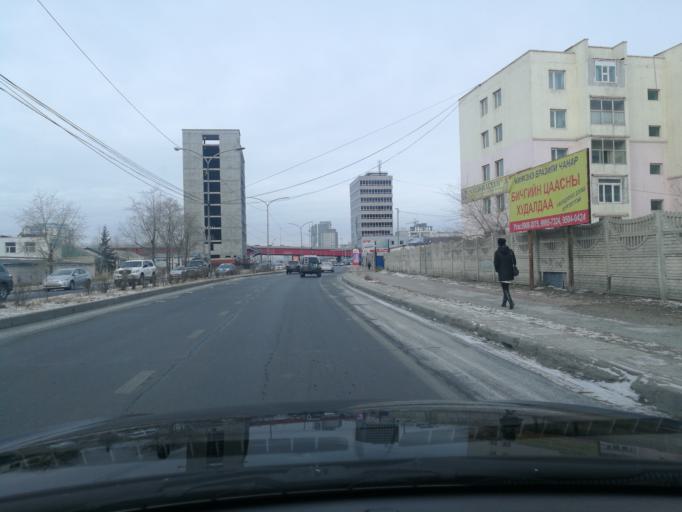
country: MN
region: Ulaanbaatar
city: Ulaanbaatar
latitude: 47.9088
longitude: 106.8987
